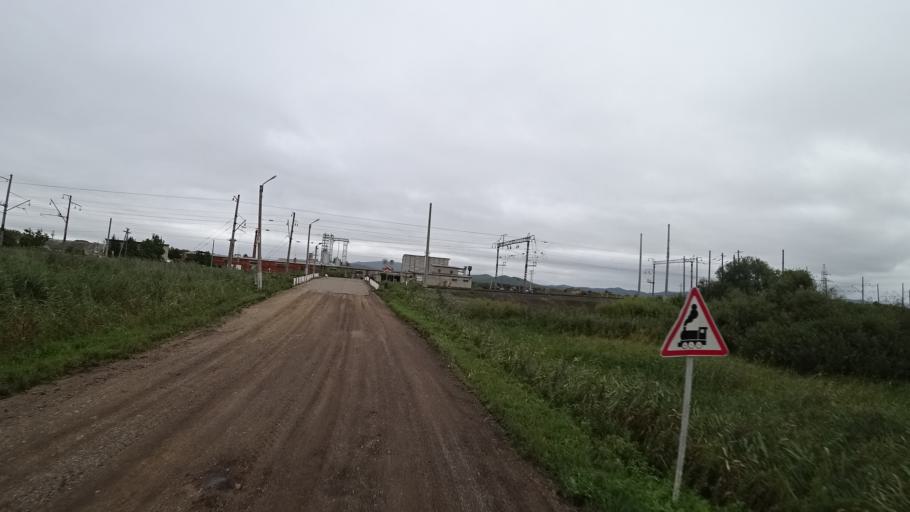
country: RU
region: Primorskiy
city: Chernigovka
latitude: 44.3337
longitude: 132.5228
